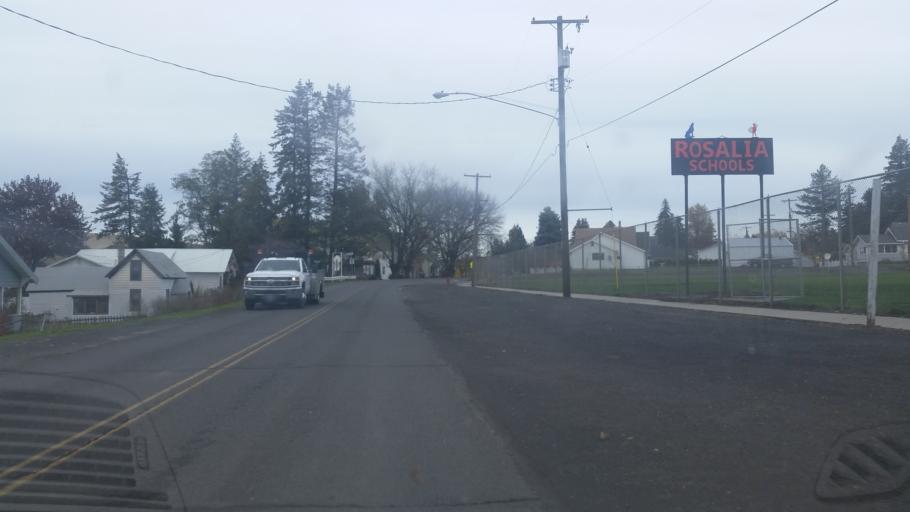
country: US
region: Washington
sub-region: Spokane County
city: Cheney
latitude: 47.2309
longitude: -117.3700
